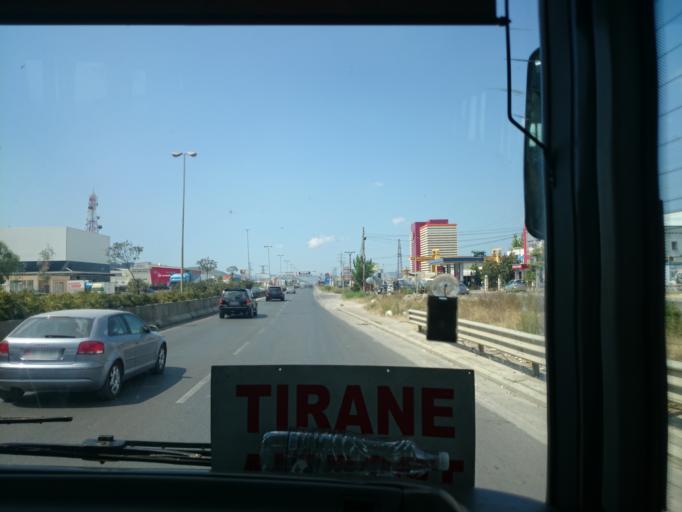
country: AL
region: Tirane
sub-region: Rrethi i Tiranes
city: Kamez
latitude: 41.3458
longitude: 19.7676
